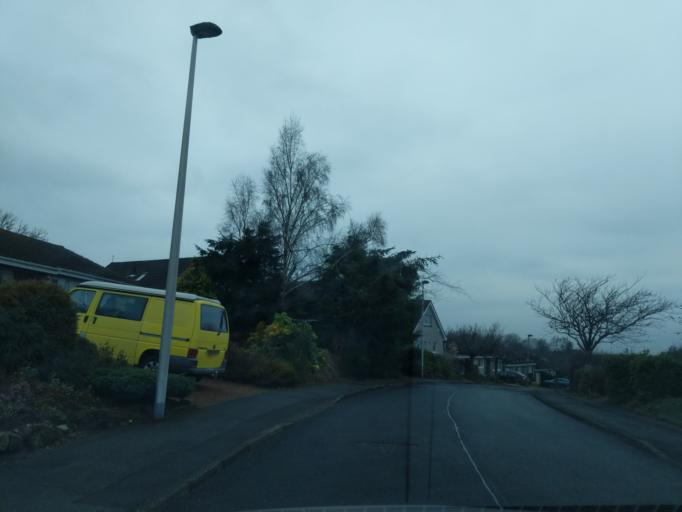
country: GB
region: Scotland
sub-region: Edinburgh
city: Balerno
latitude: 55.8917
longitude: -3.3270
